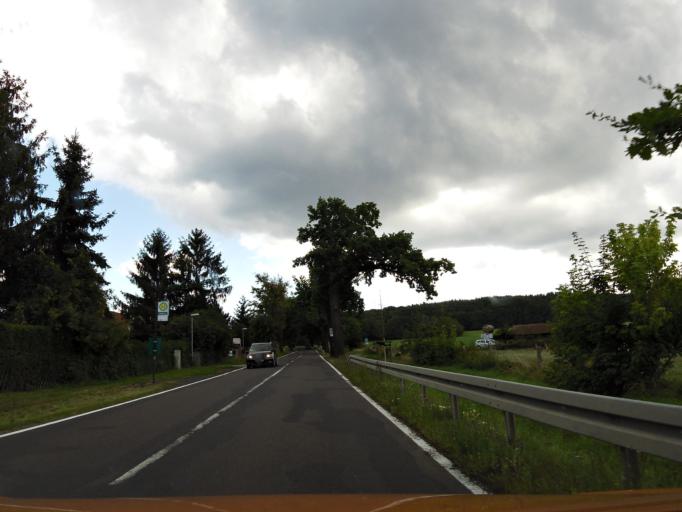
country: DE
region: Brandenburg
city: Potsdam
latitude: 52.4578
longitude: 13.0382
